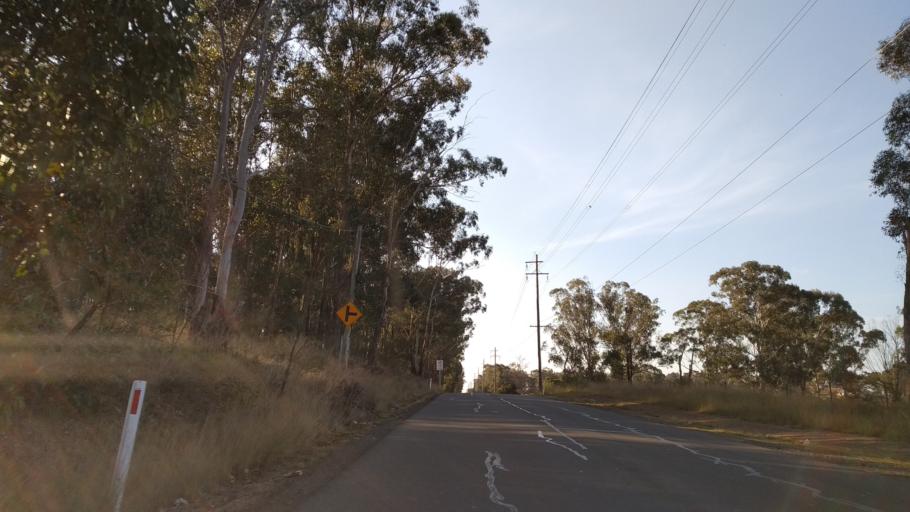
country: AU
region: New South Wales
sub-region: Penrith Municipality
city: Werrington Downs
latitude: -33.7106
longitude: 150.7318
